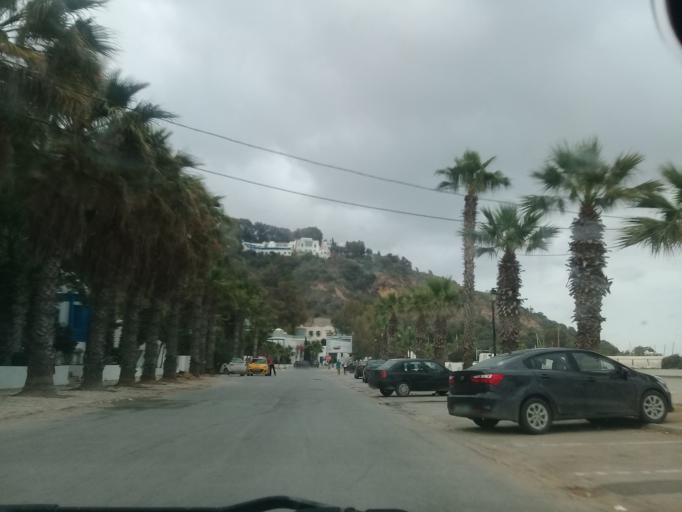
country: TN
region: Tunis
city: Sidi Bou Said
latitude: 36.8666
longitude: 10.3485
